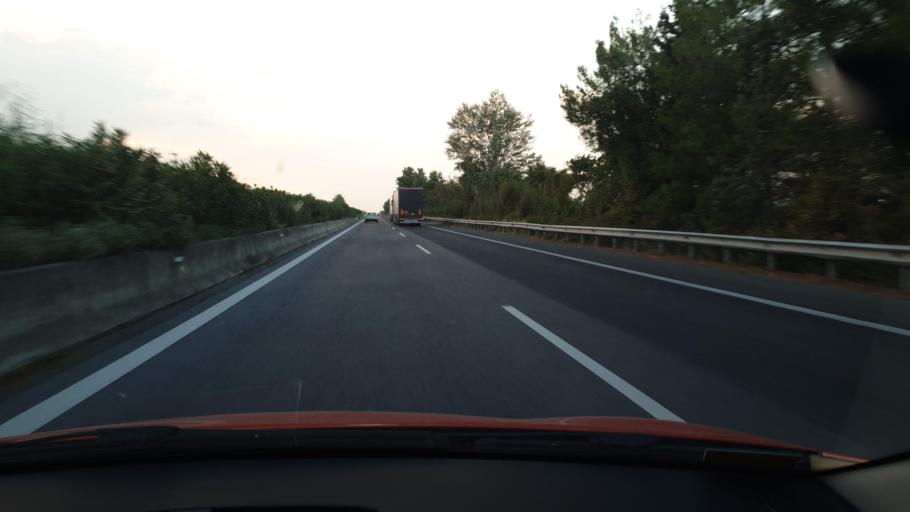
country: GR
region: Thessaly
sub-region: Nomos Magnisias
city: Stefanoviki
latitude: 39.4709
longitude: 22.6609
